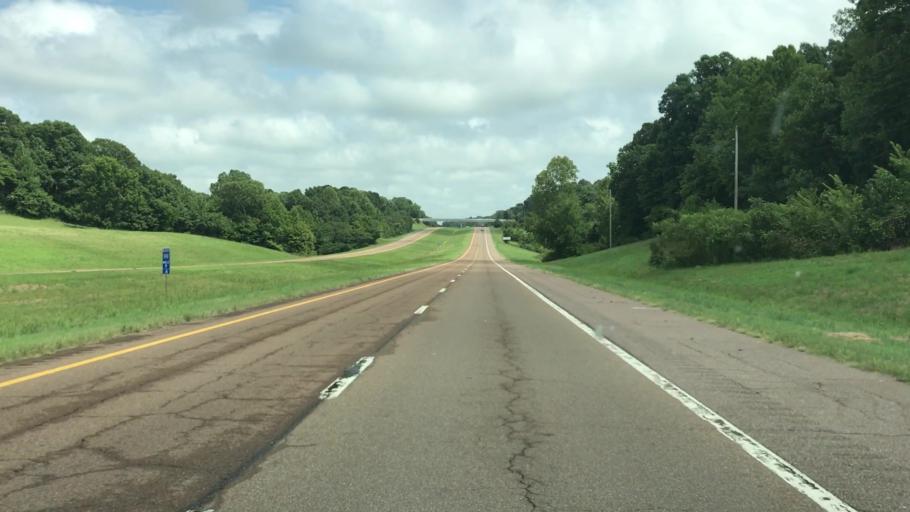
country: US
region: Tennessee
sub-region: Dyer County
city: Dyersburg
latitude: 36.0711
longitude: -89.4603
